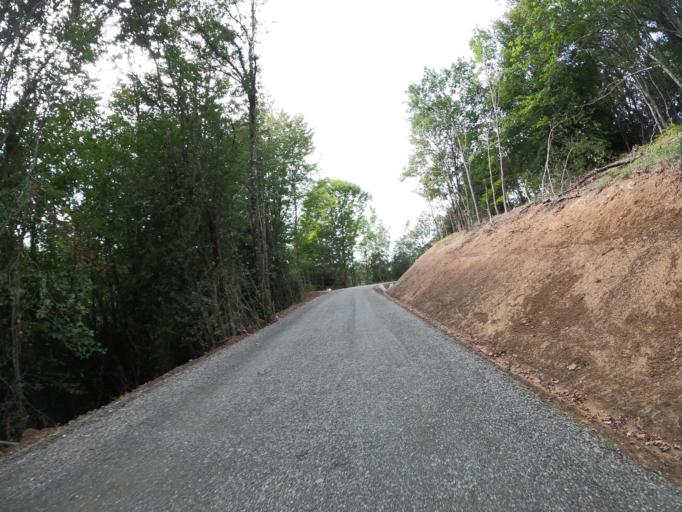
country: ES
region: Navarre
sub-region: Provincia de Navarra
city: Lekunberri
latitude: 43.0163
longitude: -1.9016
